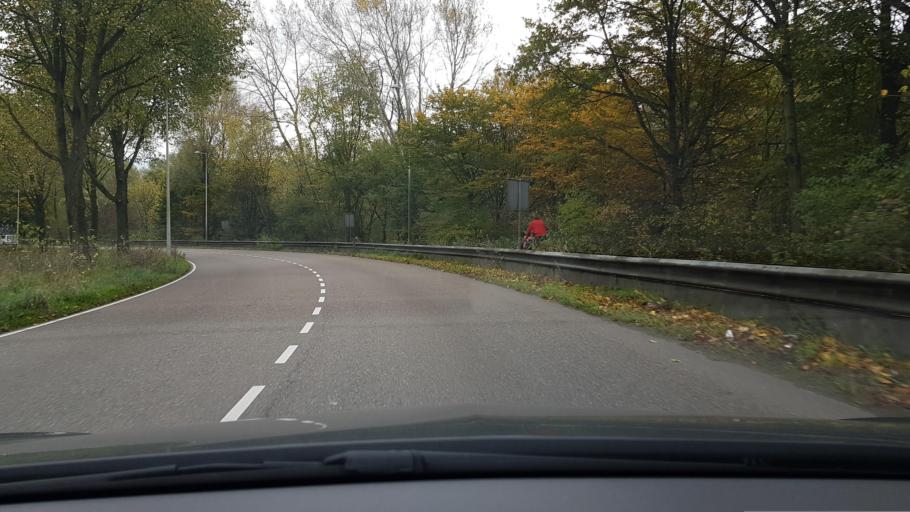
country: NL
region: North Holland
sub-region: Gemeente Zaanstad
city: Zaandam
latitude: 52.3881
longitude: 4.7946
